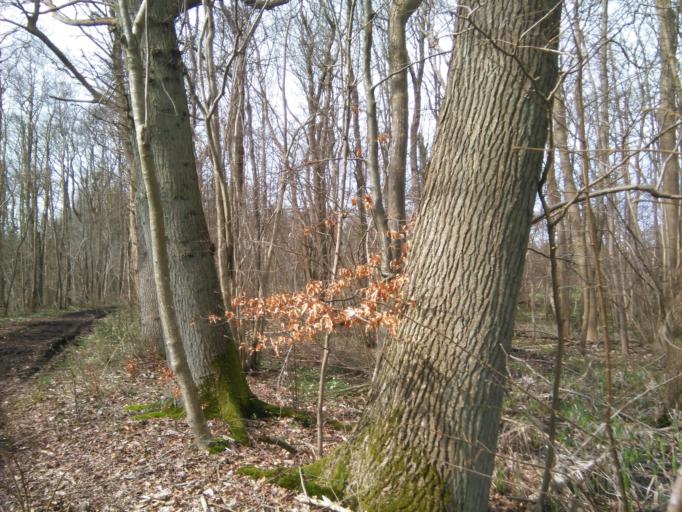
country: DK
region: Central Jutland
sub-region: Odder Kommune
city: Odder
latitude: 55.8848
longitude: 10.1064
